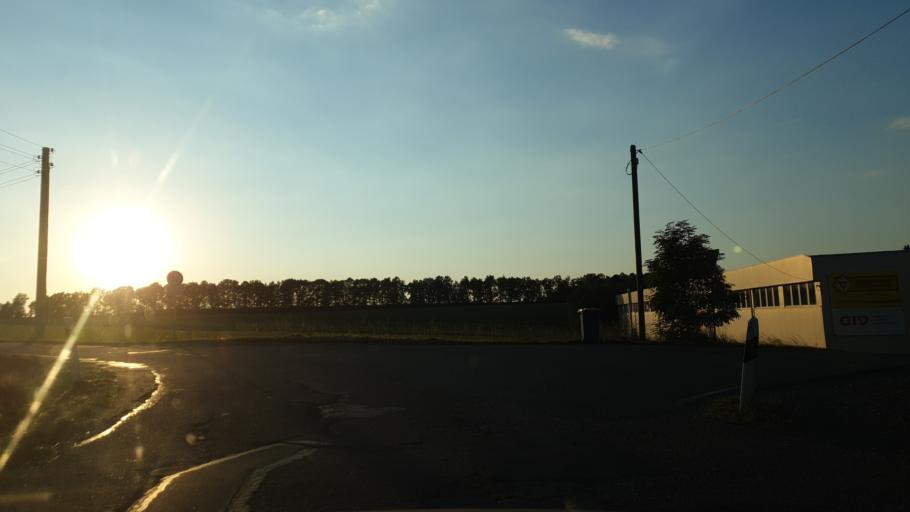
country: DE
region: Saxony
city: Stollberg
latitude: 50.6836
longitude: 12.7386
